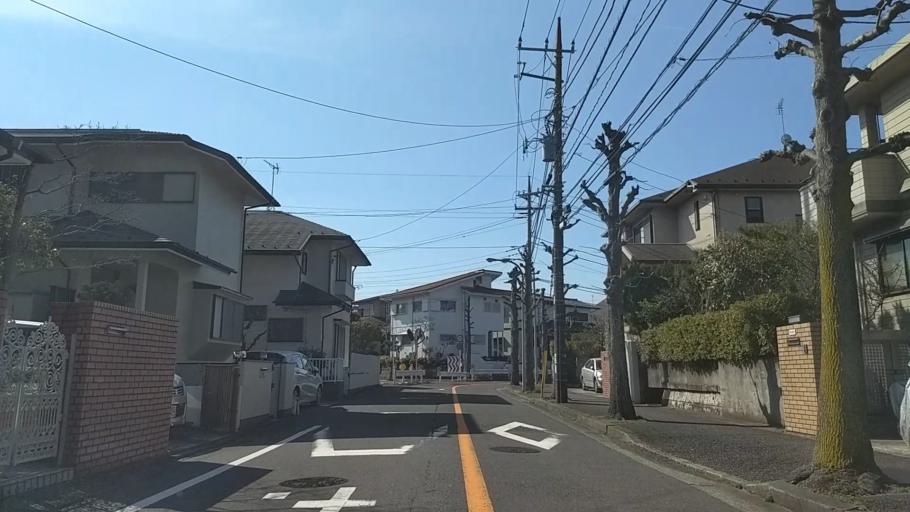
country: JP
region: Kanagawa
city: Kamakura
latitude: 35.3755
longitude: 139.5495
